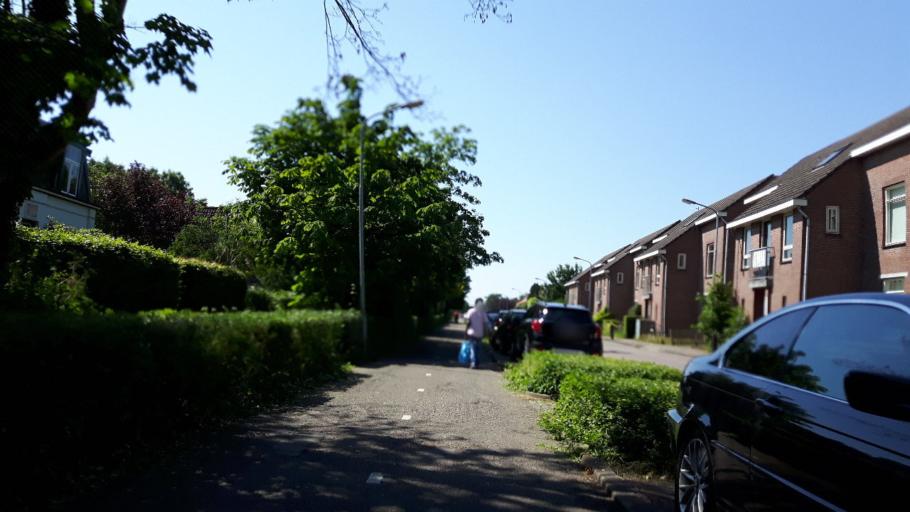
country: NL
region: North Holland
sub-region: Gemeente Wijdemeren
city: Kortenhoef
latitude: 52.2488
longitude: 5.1202
